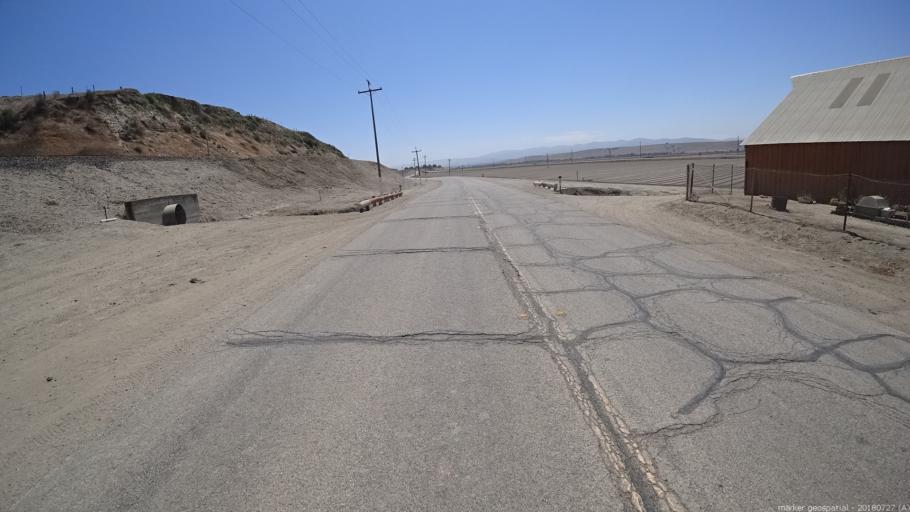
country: US
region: California
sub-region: Monterey County
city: King City
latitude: 36.1796
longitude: -121.0607
